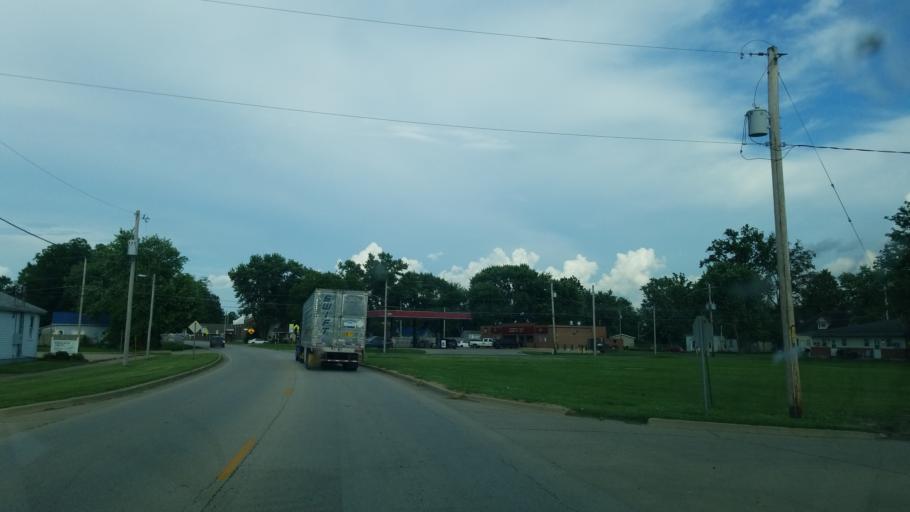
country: US
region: Illinois
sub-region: Marion County
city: Sandoval
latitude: 38.6156
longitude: -89.1191
